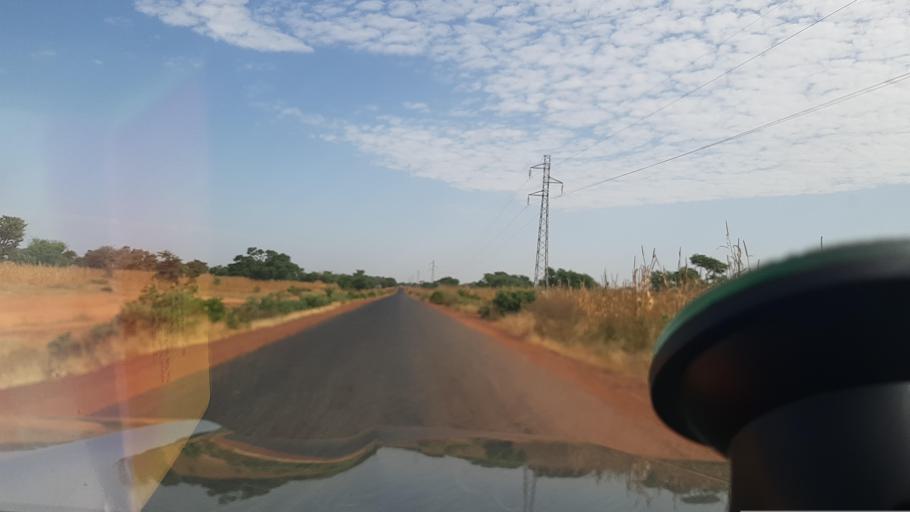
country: ML
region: Segou
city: Markala
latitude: 13.5609
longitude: -6.1117
